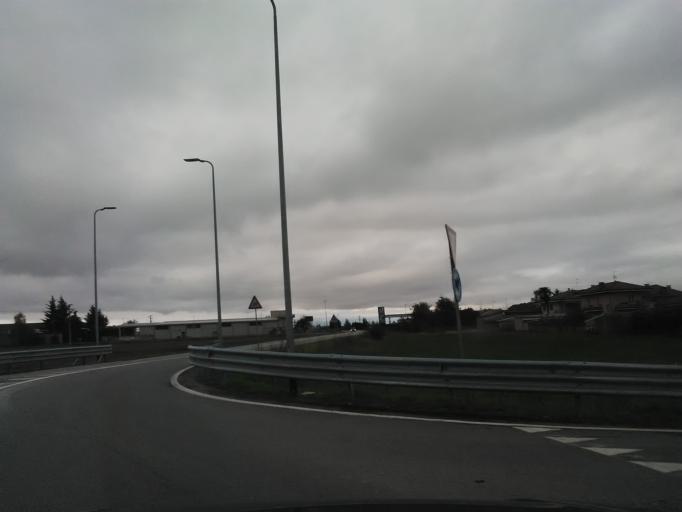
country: IT
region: Piedmont
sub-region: Provincia di Vercelli
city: Tronzano Vercellese
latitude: 45.3430
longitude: 8.1639
